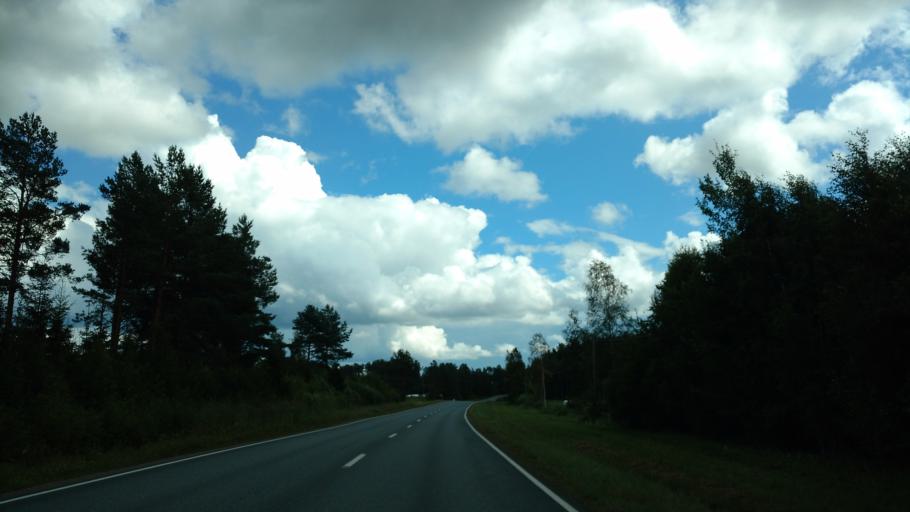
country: FI
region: Varsinais-Suomi
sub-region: Salo
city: Kisko
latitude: 60.2442
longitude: 23.5363
